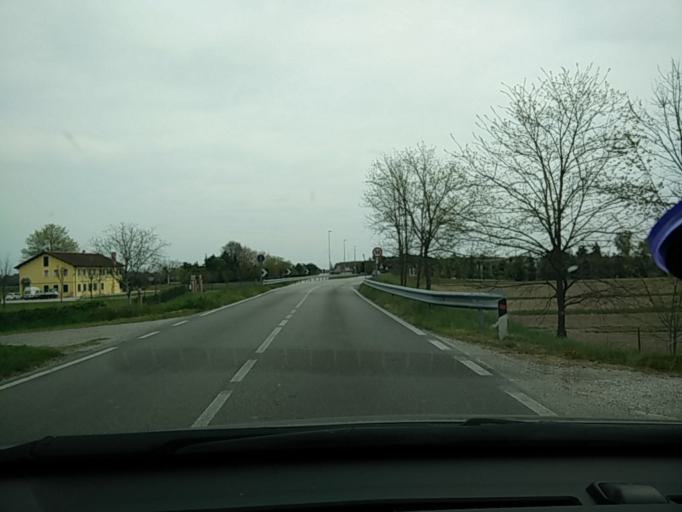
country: IT
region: Veneto
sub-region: Provincia di Venezia
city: Musile di Piave
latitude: 45.6324
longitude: 12.5275
